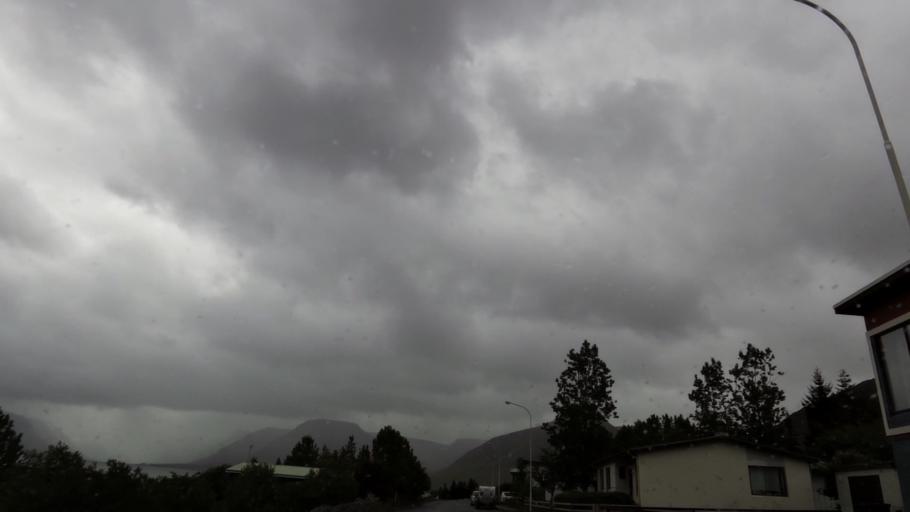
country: IS
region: Westfjords
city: Isafjoerdur
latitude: 65.8728
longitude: -23.4847
